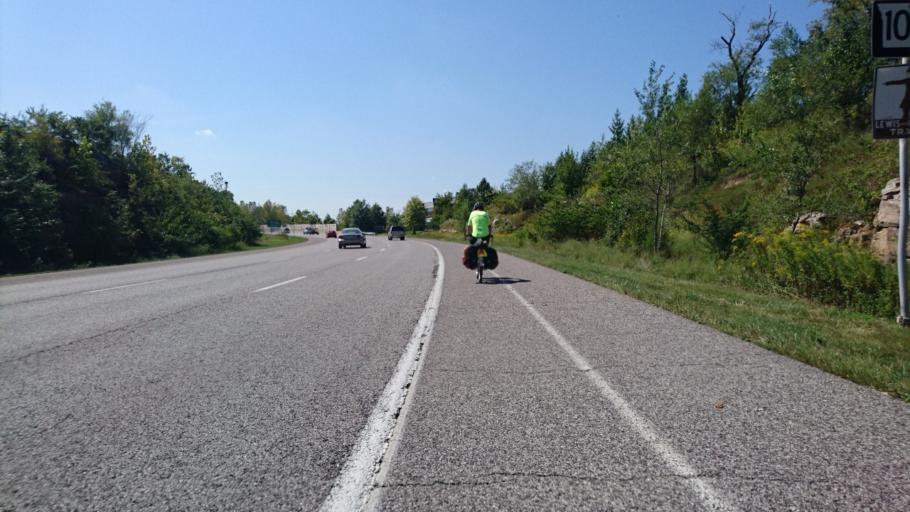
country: US
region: Missouri
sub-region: Saint Louis County
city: Town and Country
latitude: 38.6037
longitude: -90.4650
